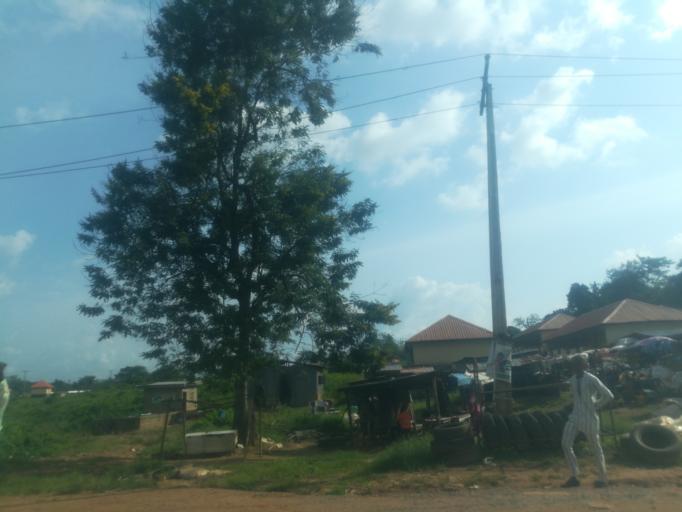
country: NG
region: Oyo
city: Ido
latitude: 7.3963
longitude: 3.7894
